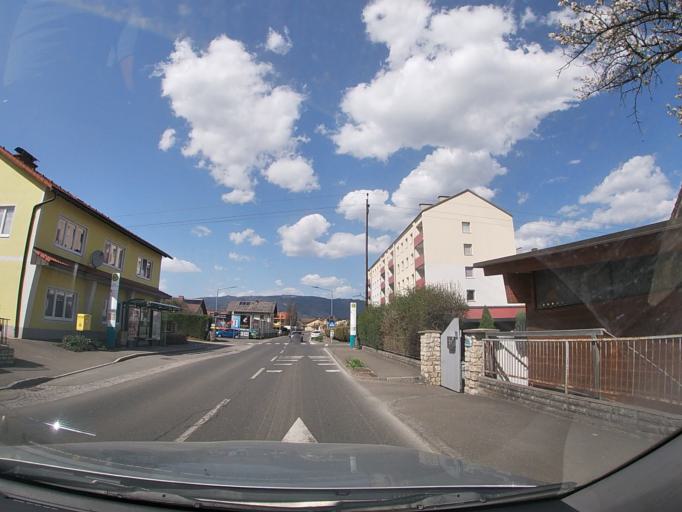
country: AT
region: Styria
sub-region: Politischer Bezirk Murtal
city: Judenburg
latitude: 47.1713
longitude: 14.6795
